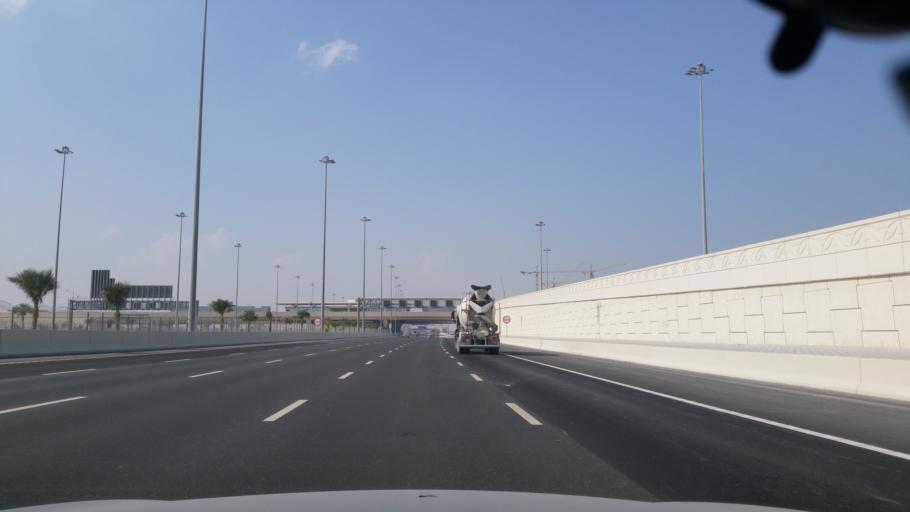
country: QA
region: Baladiyat Umm Salal
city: Umm Salal Muhammad
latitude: 25.4105
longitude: 51.4892
